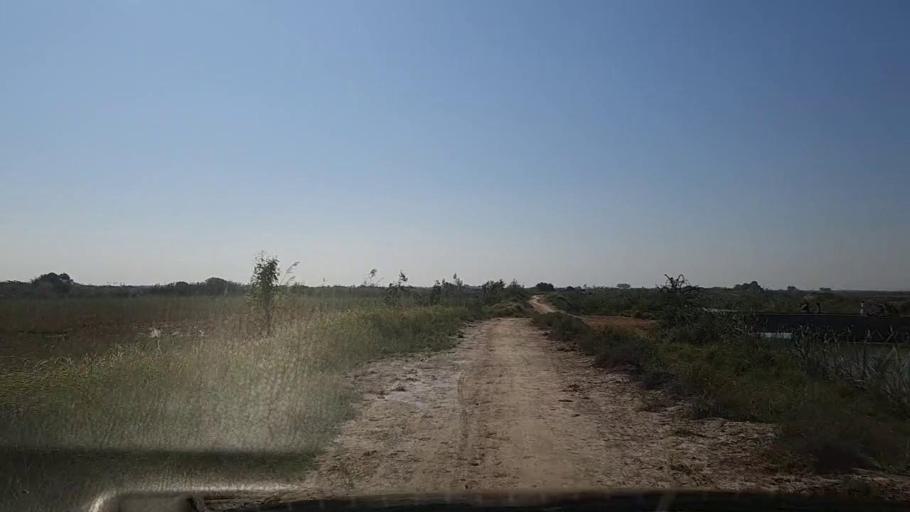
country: PK
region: Sindh
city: Thatta
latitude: 24.6699
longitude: 67.8894
